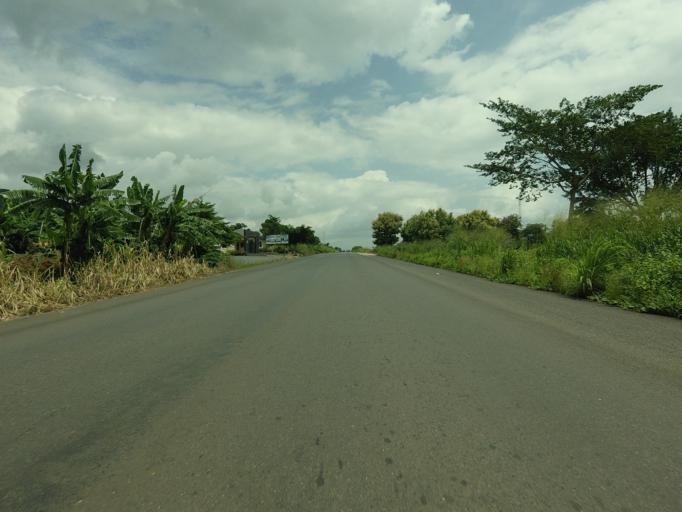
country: GH
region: Volta
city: Ho
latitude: 6.5558
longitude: 0.2598
